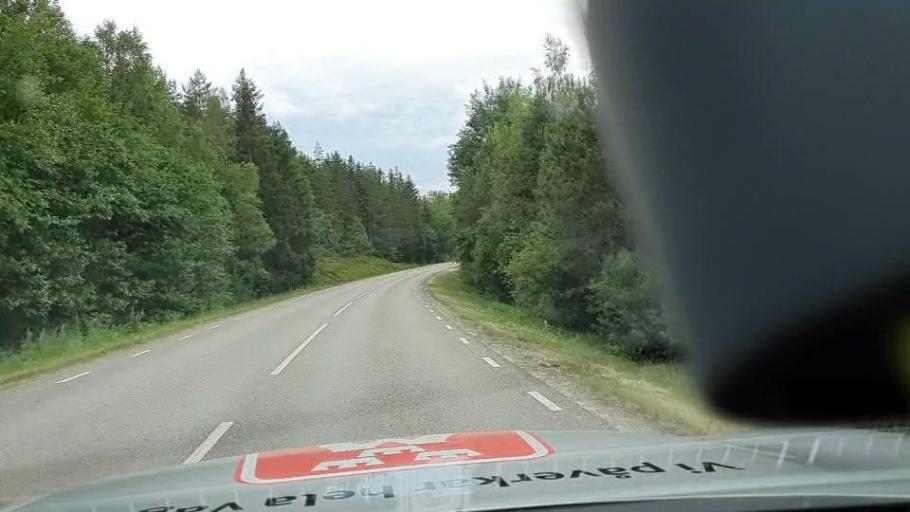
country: SE
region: Kalmar
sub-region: Emmaboda Kommun
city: Emmaboda
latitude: 56.5313
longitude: 15.5455
